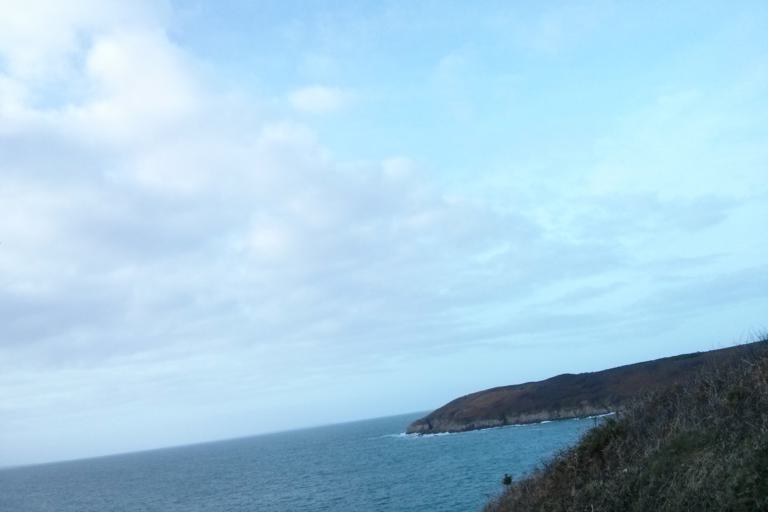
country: FR
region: Brittany
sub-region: Departement du Finistere
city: Le Conquet
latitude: 48.4011
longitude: -4.7745
